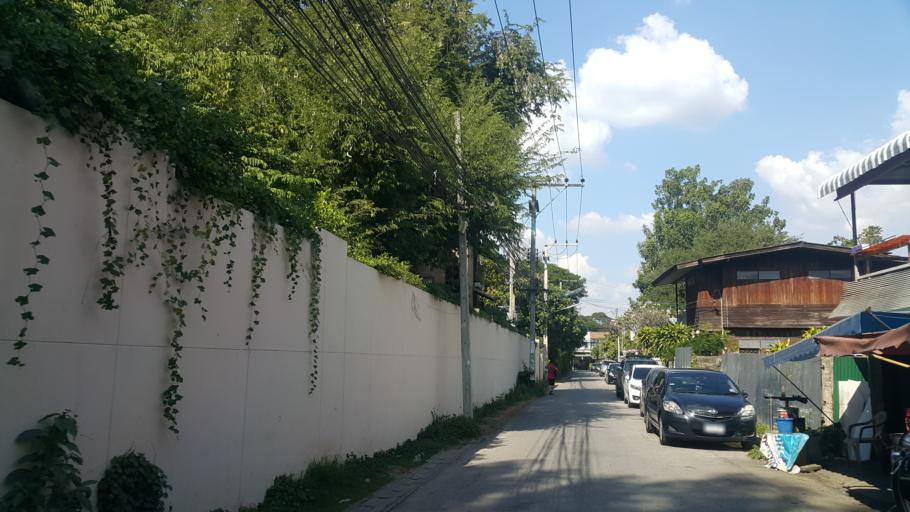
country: TH
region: Chiang Mai
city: Chiang Mai
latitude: 18.7725
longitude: 99.0157
